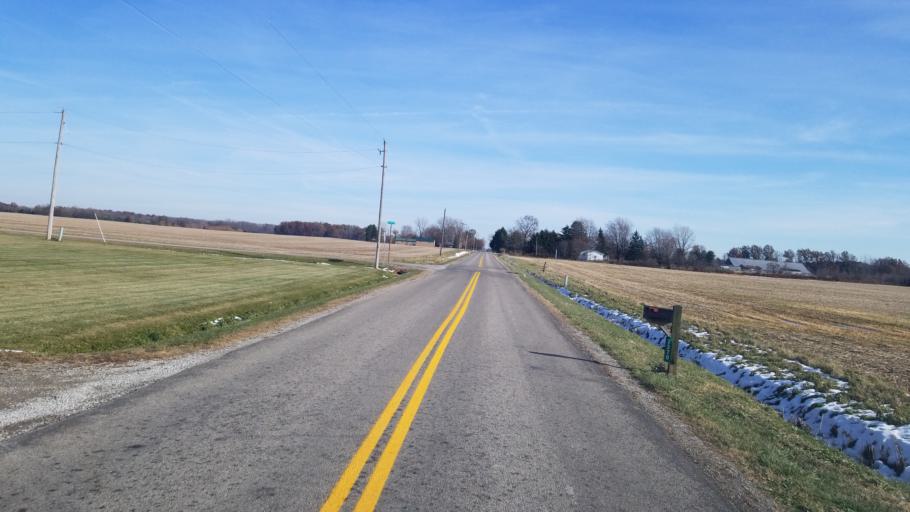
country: US
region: Ohio
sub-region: Huron County
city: Norwalk
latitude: 41.2038
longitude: -82.5095
